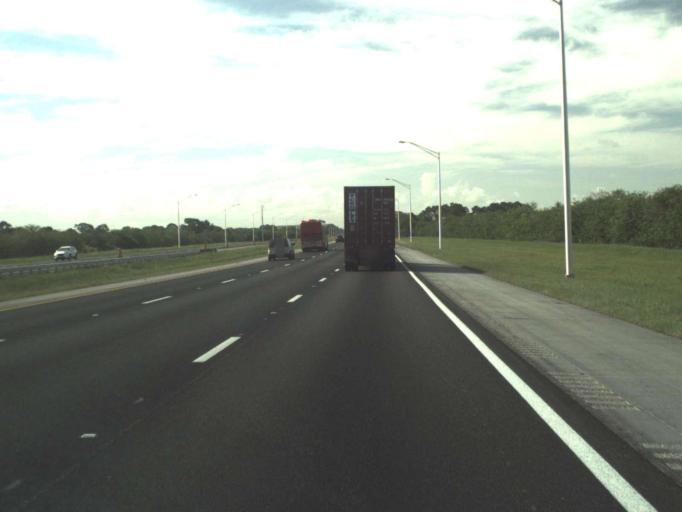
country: US
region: Florida
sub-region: Indian River County
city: West Vero Corridor
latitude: 27.6066
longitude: -80.5101
